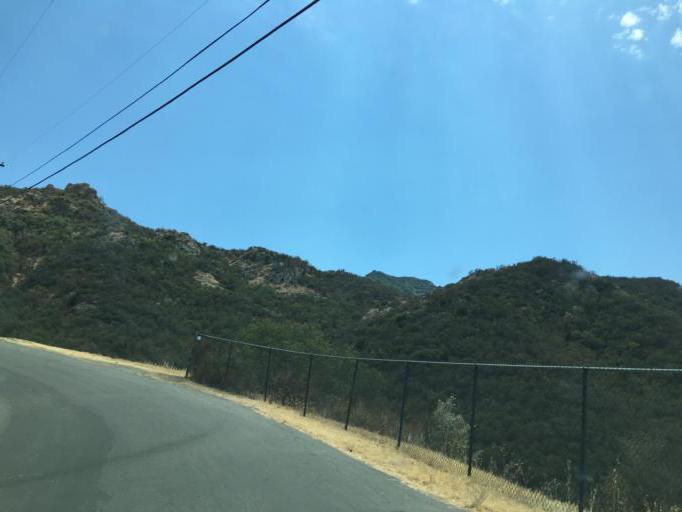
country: US
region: California
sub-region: Los Angeles County
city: Agoura Hills
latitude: 34.1026
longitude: -118.7593
